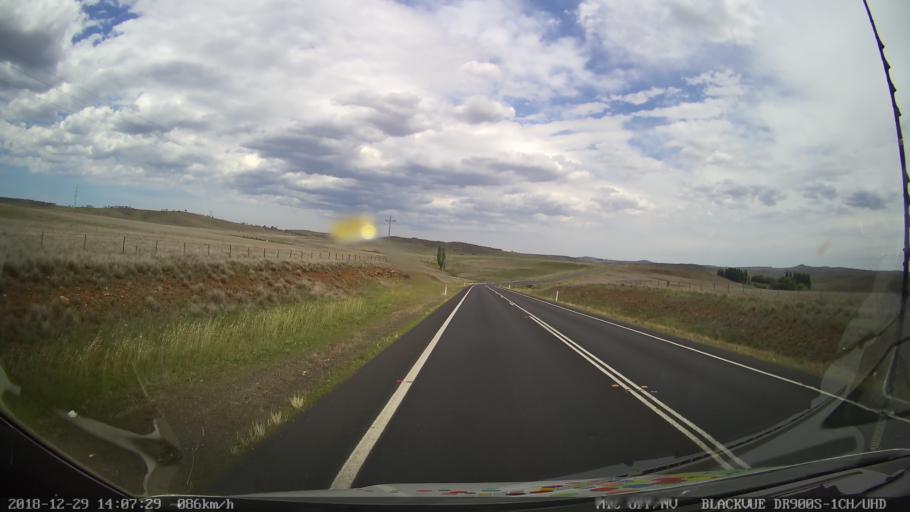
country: AU
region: New South Wales
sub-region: Cooma-Monaro
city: Cooma
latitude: -36.3524
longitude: 149.2140
